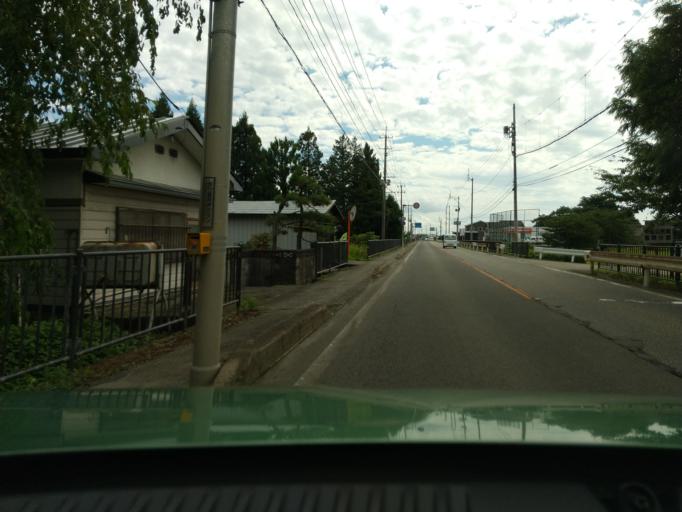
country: JP
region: Akita
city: Kakunodatemachi
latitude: 39.5704
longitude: 140.5614
